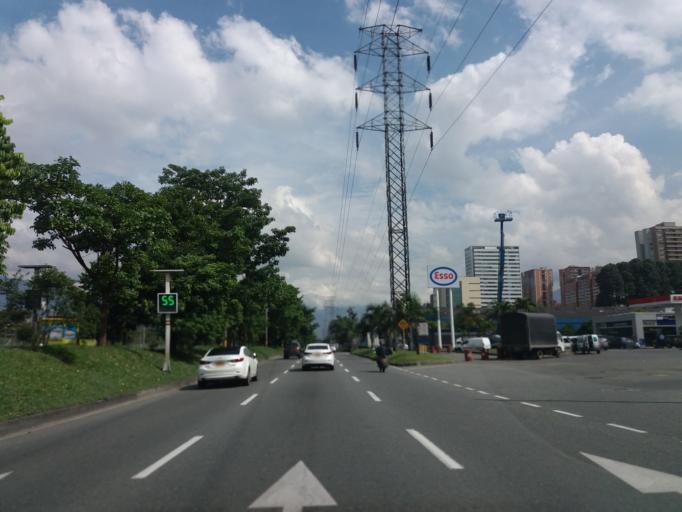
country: CO
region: Antioquia
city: Medellin
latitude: 6.2179
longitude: -75.5769
